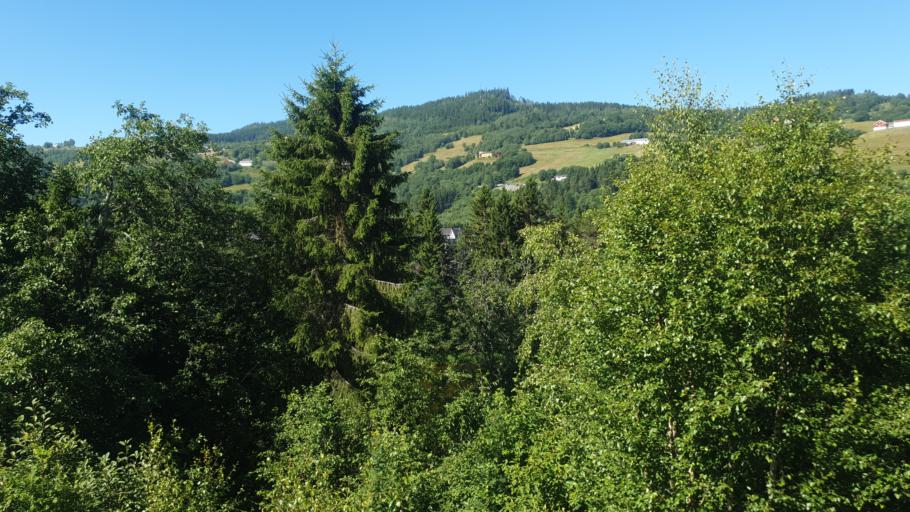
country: NO
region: Sor-Trondelag
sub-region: Meldal
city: Meldal
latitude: 63.1700
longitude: 9.7485
